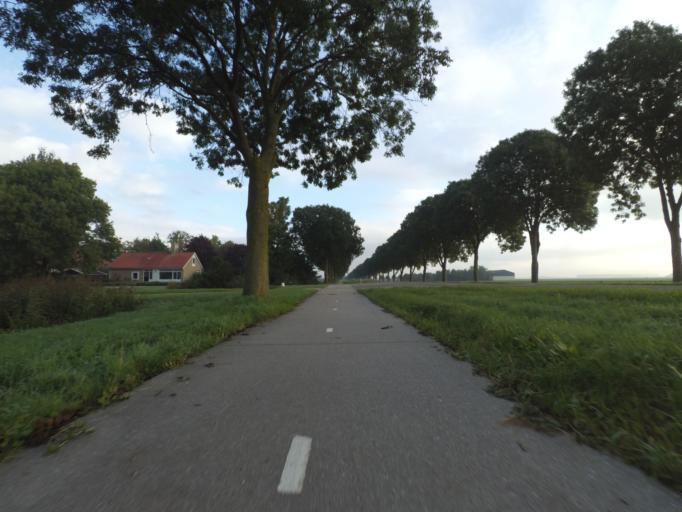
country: NL
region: Flevoland
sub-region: Gemeente Dronten
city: Biddinghuizen
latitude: 52.4852
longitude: 5.6680
